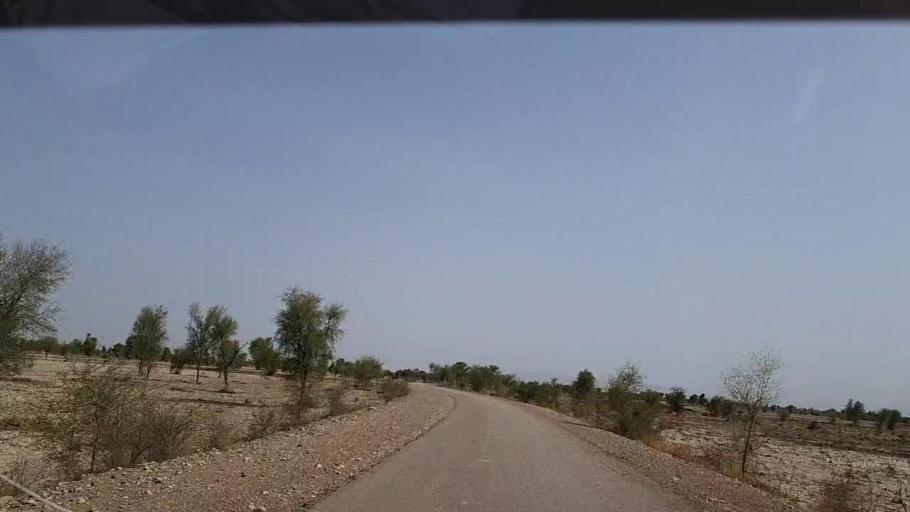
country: PK
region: Sindh
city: Johi
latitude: 26.6450
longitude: 67.5036
